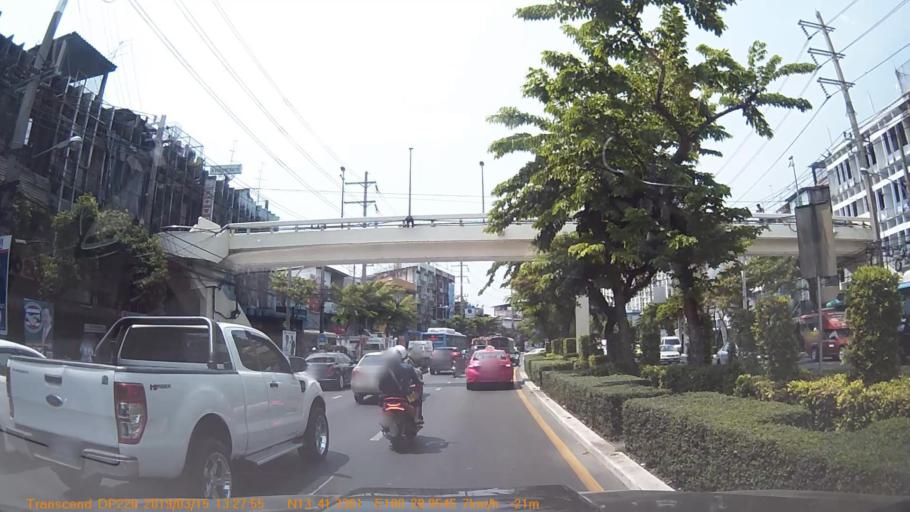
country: TH
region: Bangkok
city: Chom Thong
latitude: 13.6890
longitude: 100.4826
